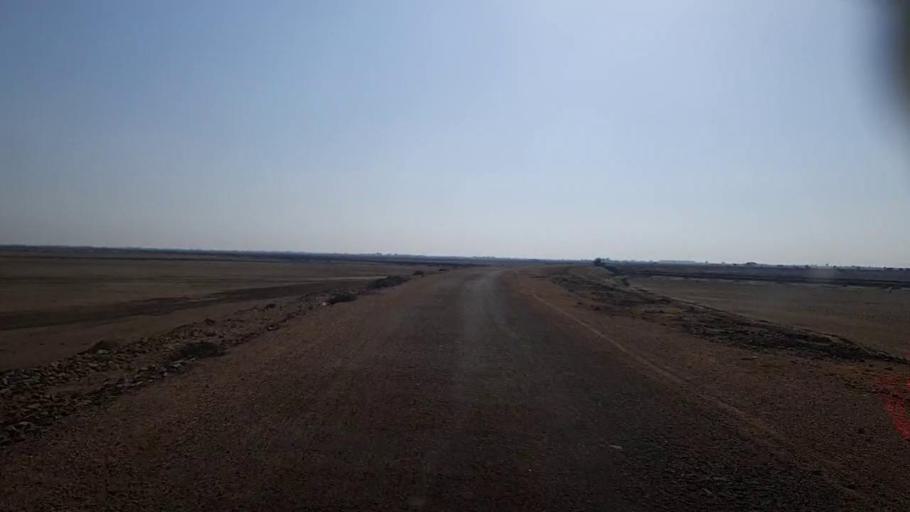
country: PK
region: Sindh
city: Mirpur Sakro
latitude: 24.5168
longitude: 67.5025
